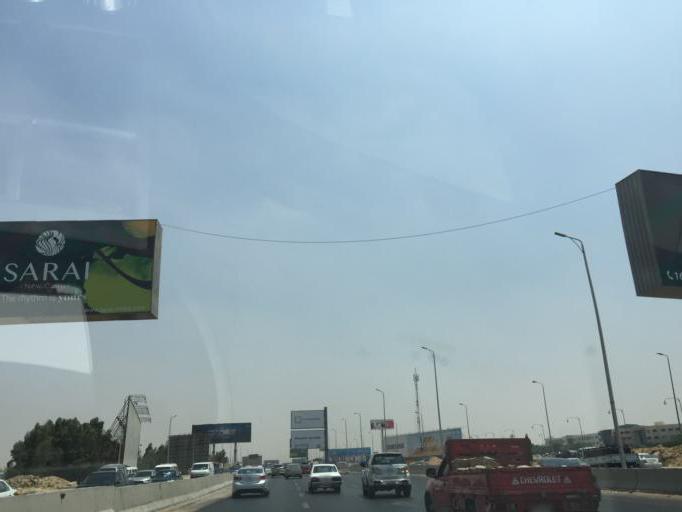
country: EG
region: Muhafazat al Qalyubiyah
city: Al Khankah
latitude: 30.0554
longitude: 31.4124
